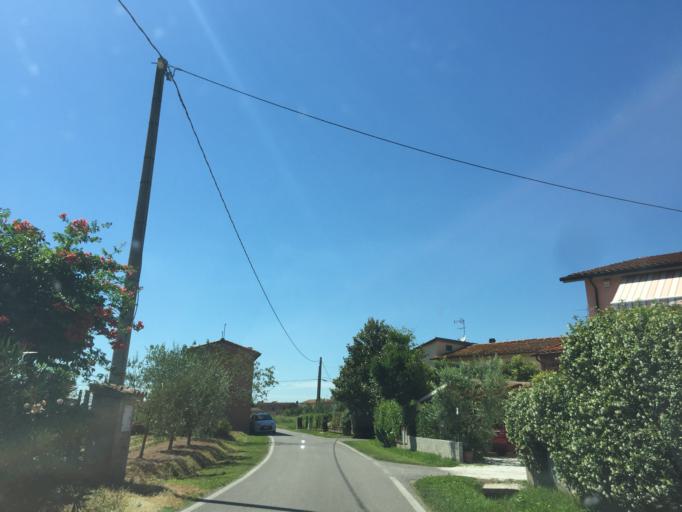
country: IT
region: Tuscany
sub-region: Provincia di Pistoia
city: Anchione
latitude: 43.8297
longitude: 10.7469
